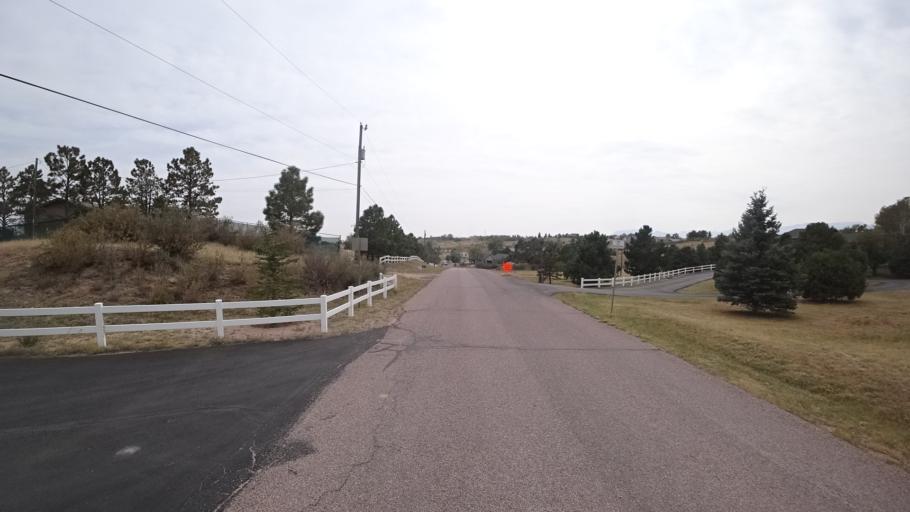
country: US
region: Colorado
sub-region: El Paso County
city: Cimarron Hills
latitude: 38.8981
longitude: -104.7243
